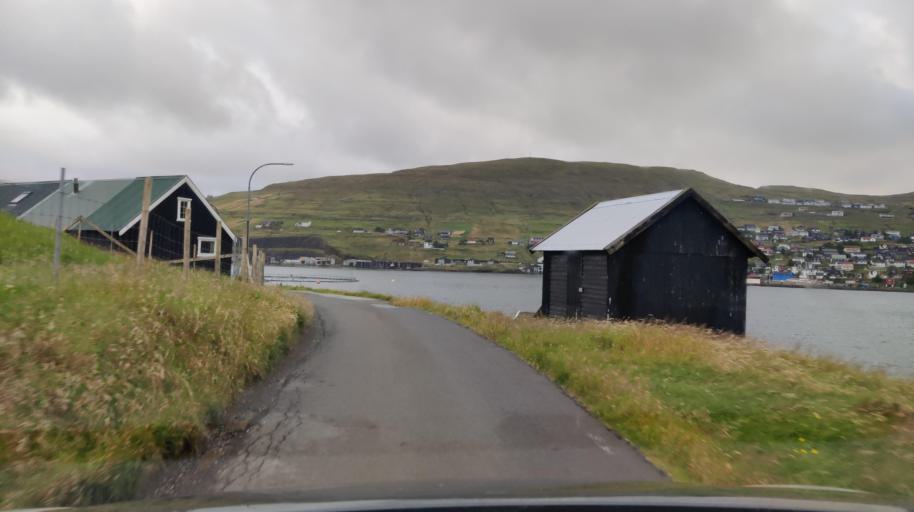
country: FO
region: Streymoy
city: Vestmanna
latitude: 62.1501
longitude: -7.1589
